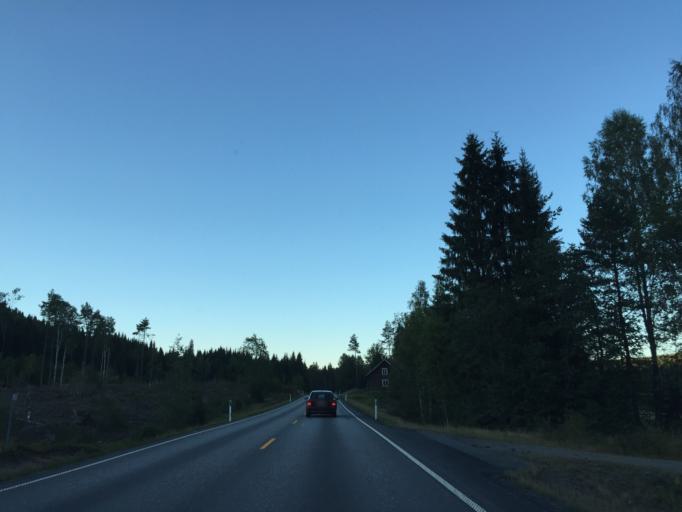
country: NO
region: Hedmark
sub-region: Nord-Odal
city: Sand
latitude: 60.4908
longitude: 11.5003
